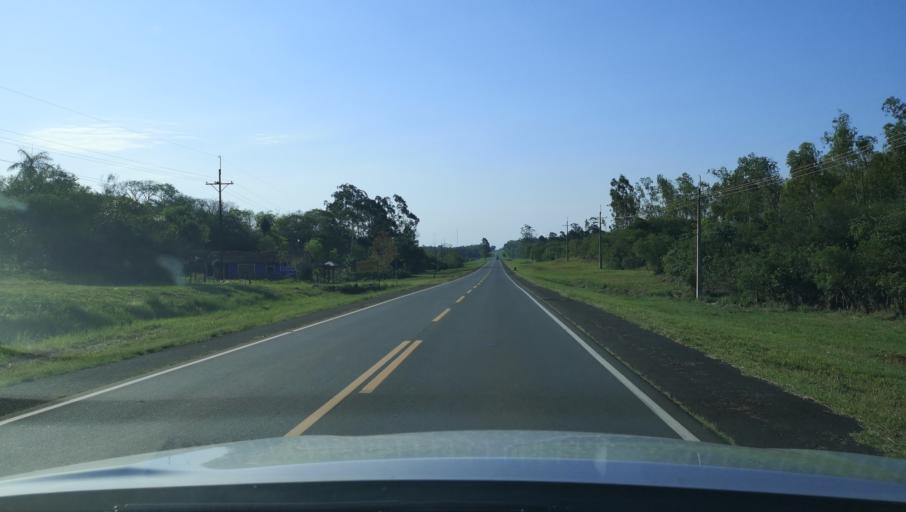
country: PY
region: Misiones
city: Santa Maria
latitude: -26.7561
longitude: -57.0364
